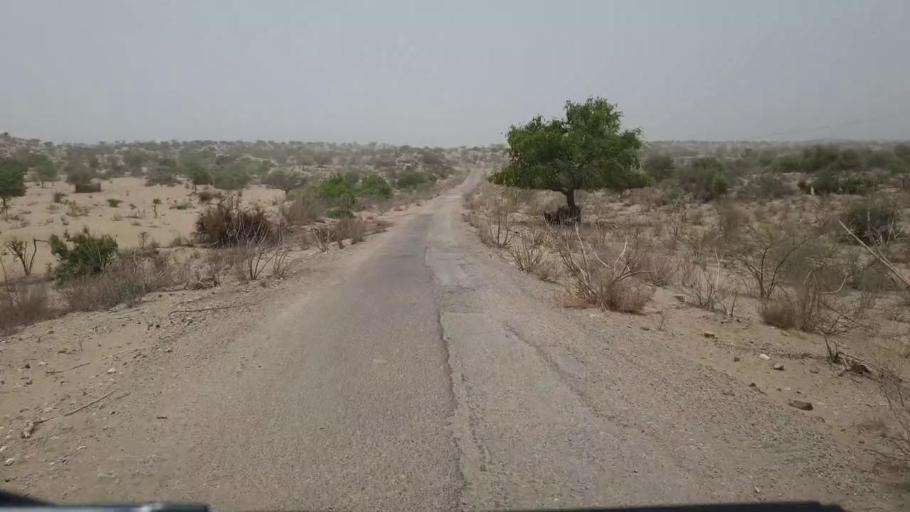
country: PK
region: Sindh
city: Naukot
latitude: 24.7408
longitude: 69.5478
